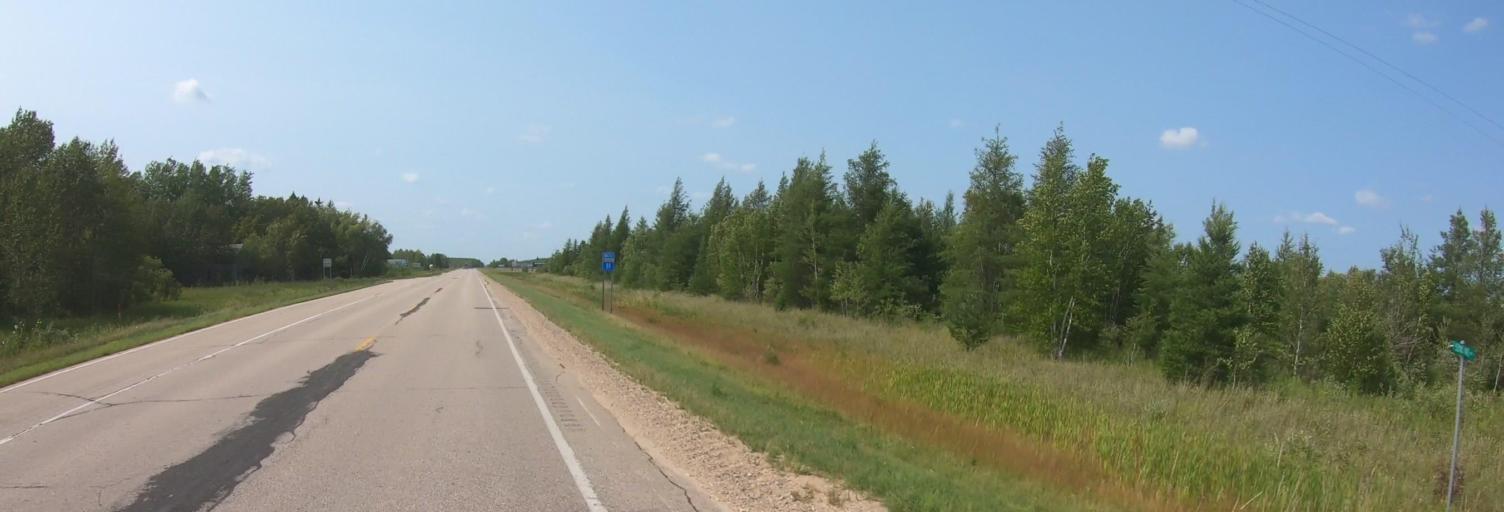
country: US
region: Minnesota
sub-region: Lake of the Woods County
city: Baudette
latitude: 48.7398
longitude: -94.8375
